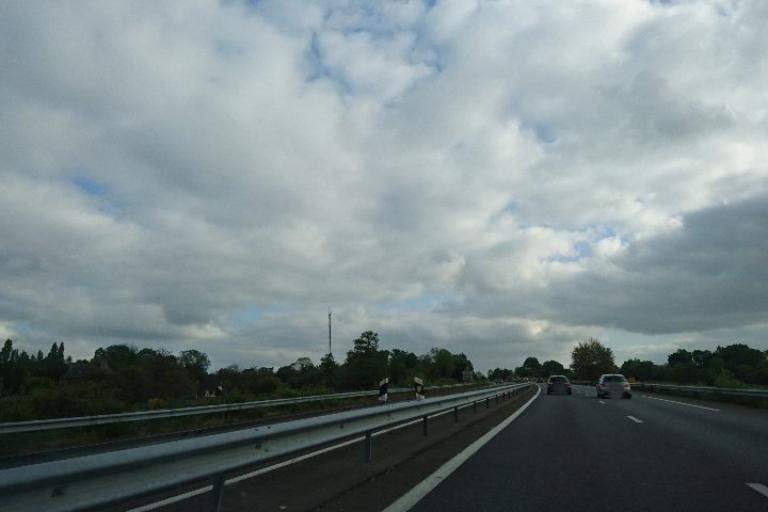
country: FR
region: Brittany
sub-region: Departement d'Ille-et-Vilaine
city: Saint-Pierre-de-Plesguen
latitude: 48.4488
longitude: -1.9239
